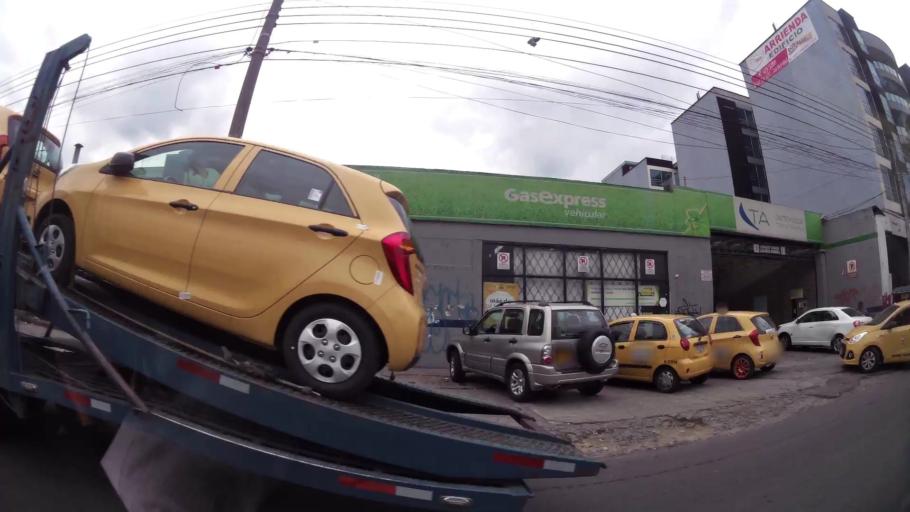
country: CO
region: Bogota D.C.
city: Barrio San Luis
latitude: 4.6644
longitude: -74.0661
